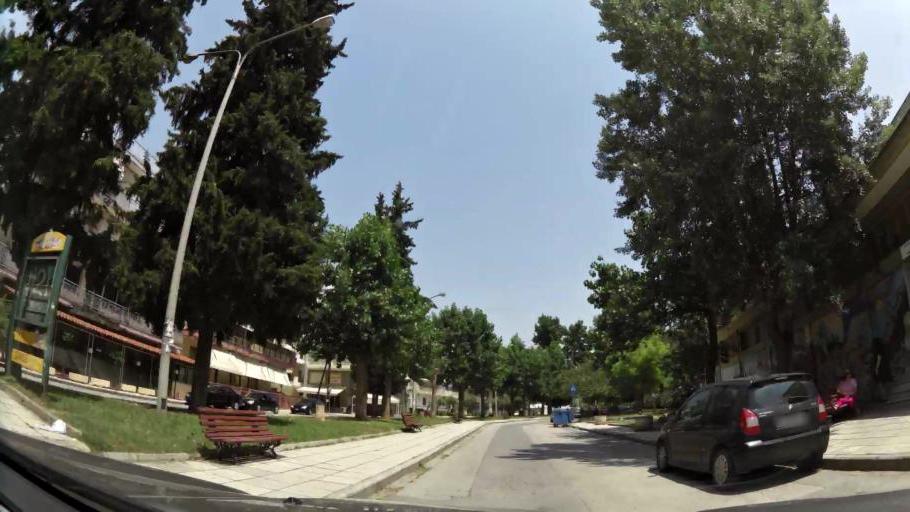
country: GR
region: Central Macedonia
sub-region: Nomos Thessalonikis
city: Evosmos
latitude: 40.6676
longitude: 22.9007
